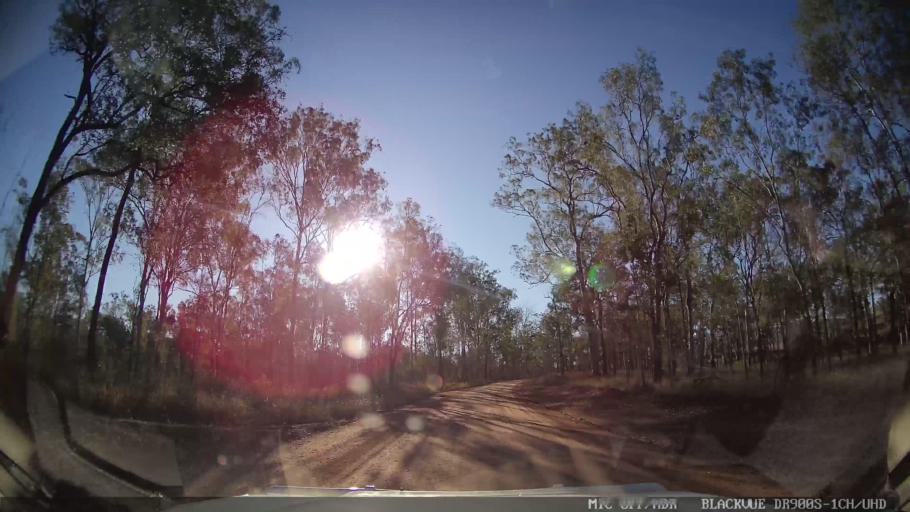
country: AU
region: Queensland
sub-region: Bundaberg
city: Sharon
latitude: -24.7388
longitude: 151.5242
